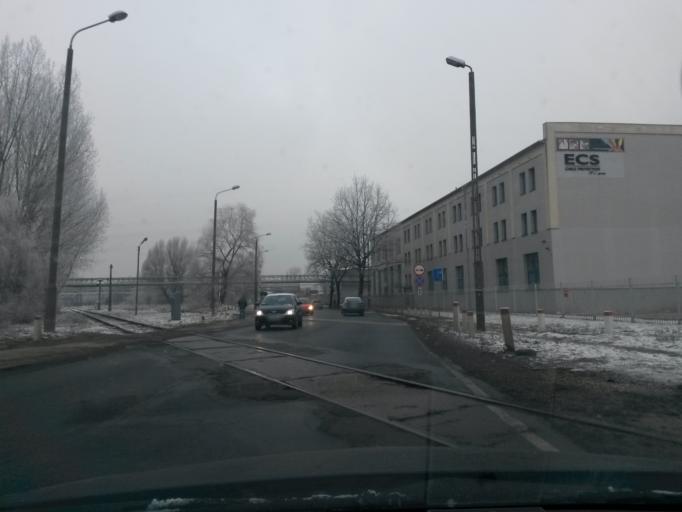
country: PL
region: Kujawsko-Pomorskie
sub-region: Powiat inowroclawski
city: Inowroclaw
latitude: 52.7486
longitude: 18.2553
